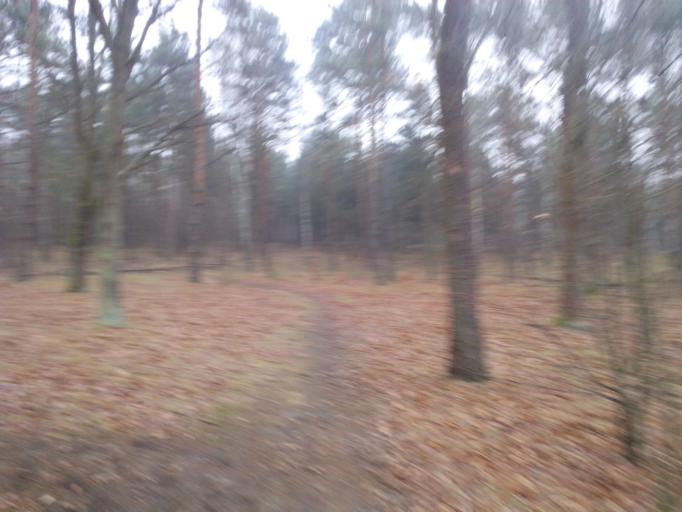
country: PL
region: Masovian Voivodeship
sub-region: Warszawa
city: Bialoleka
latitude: 52.3369
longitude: 20.9725
